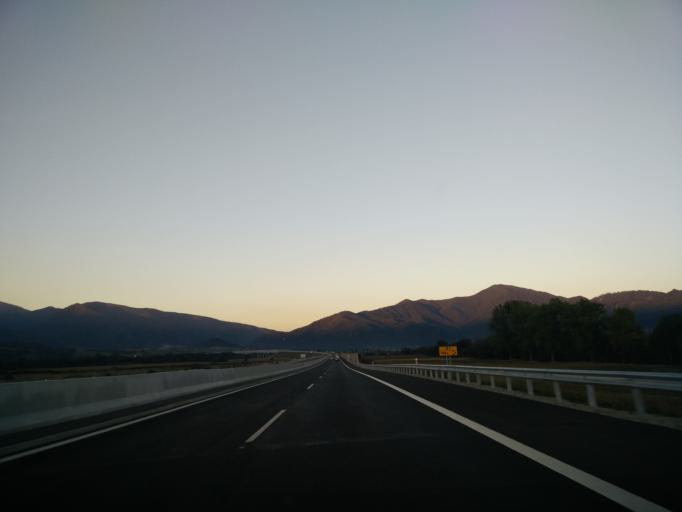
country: SK
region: Zilinsky
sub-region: Okres Martin
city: Martin
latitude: 49.1076
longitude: 19.0524
